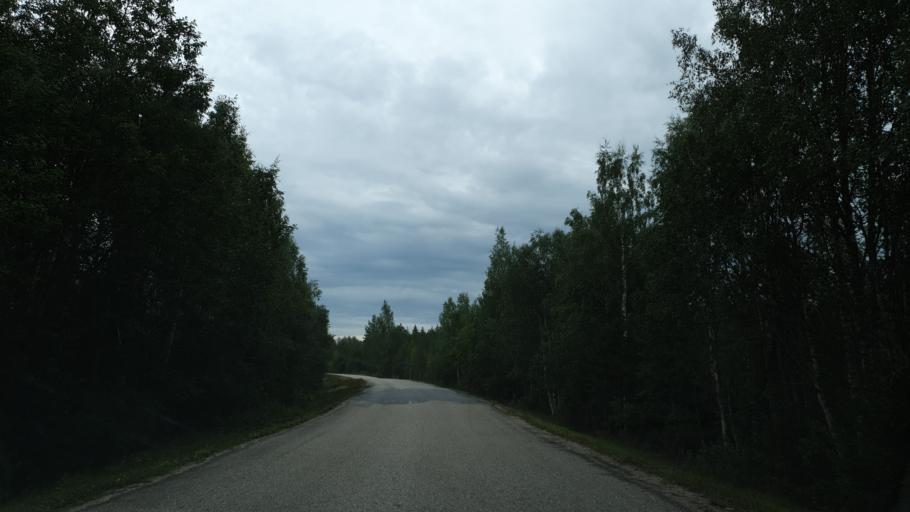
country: FI
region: Kainuu
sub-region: Kehys-Kainuu
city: Kuhmo
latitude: 64.3517
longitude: 29.1600
